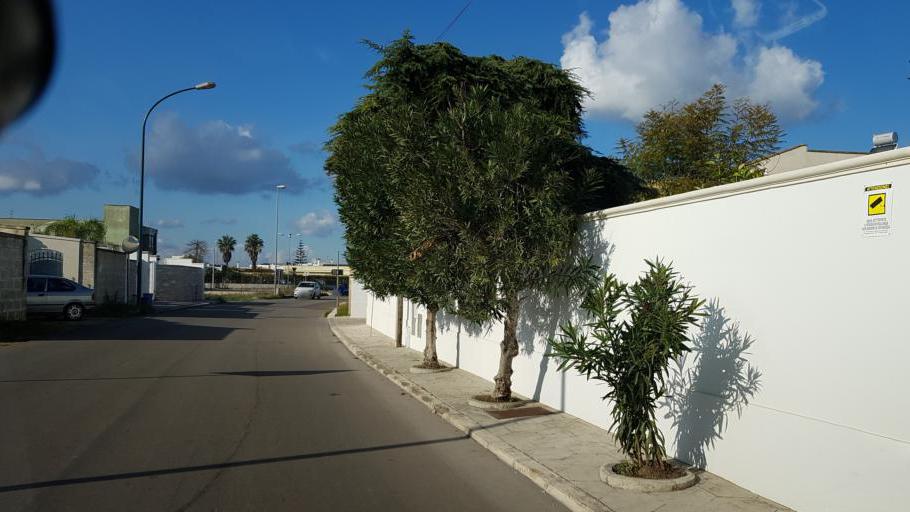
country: IT
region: Apulia
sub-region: Provincia di Lecce
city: Squinzano
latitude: 40.4271
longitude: 18.0356
